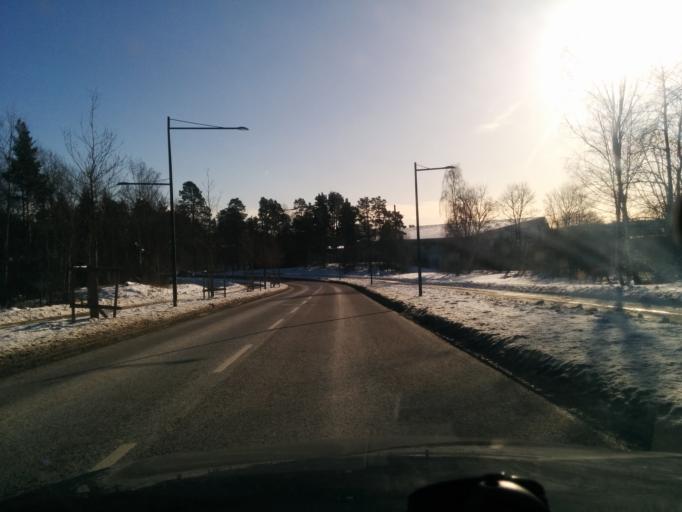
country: SE
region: Stockholm
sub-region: Taby Kommun
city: Taby
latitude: 59.4724
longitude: 18.1288
